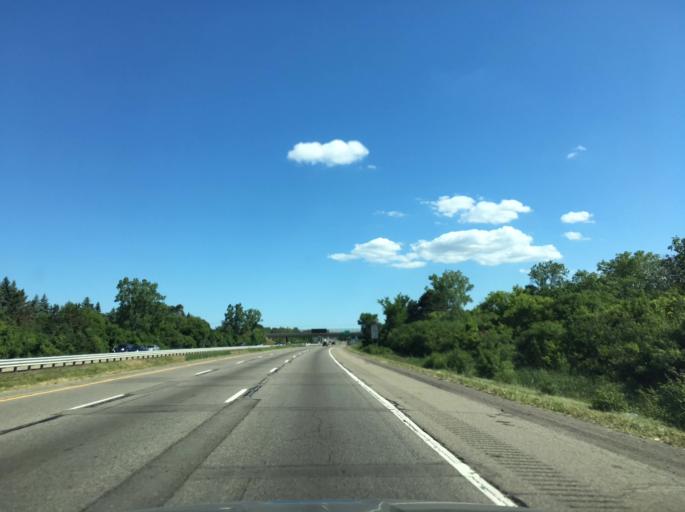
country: US
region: Michigan
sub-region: Oakland County
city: Troy
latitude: 42.5737
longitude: -83.1591
